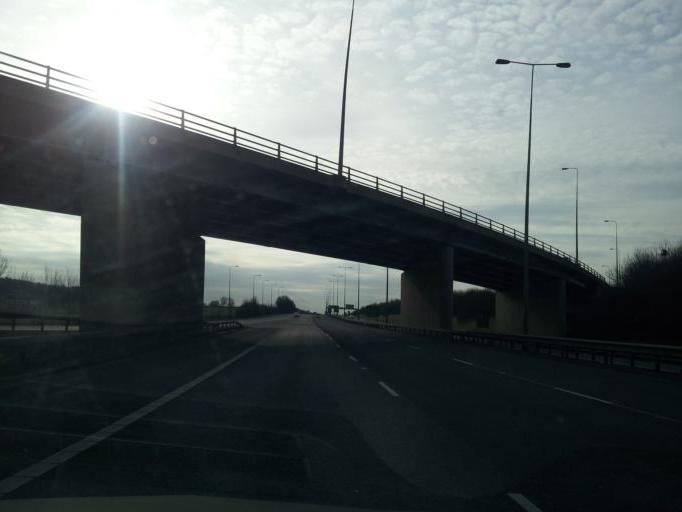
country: GB
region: England
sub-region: Peterborough
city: Castor
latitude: 52.5322
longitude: -0.3168
